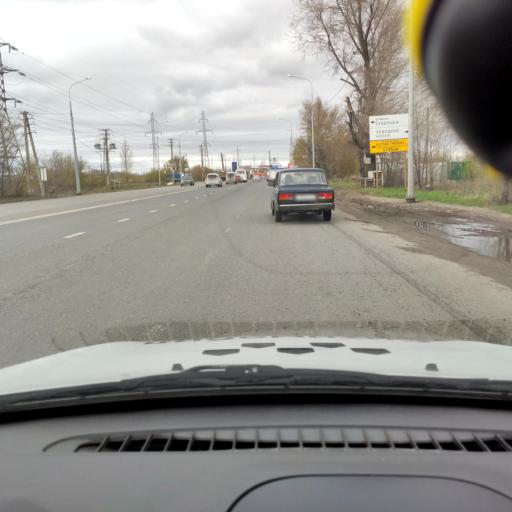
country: RU
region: Samara
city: Tol'yatti
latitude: 53.5793
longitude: 49.2947
